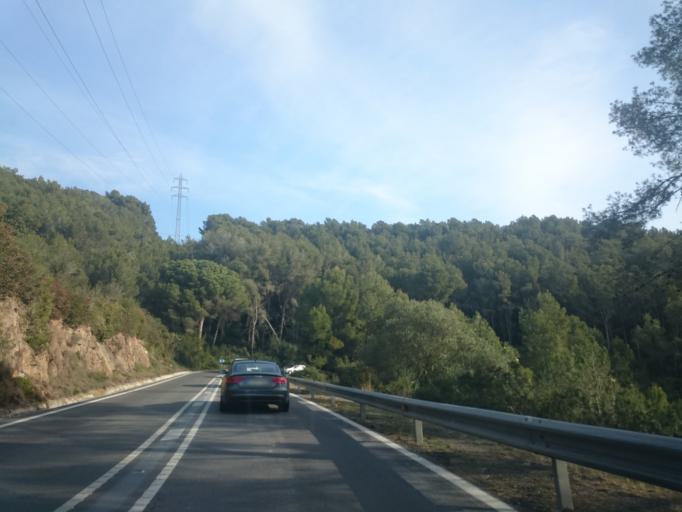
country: ES
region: Catalonia
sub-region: Provincia de Barcelona
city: Gava
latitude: 41.3083
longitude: 1.9824
